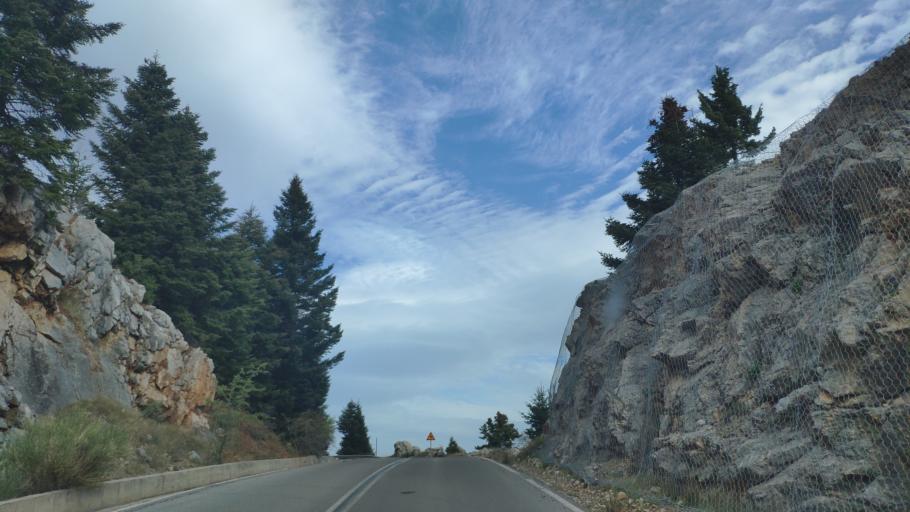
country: GR
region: Central Greece
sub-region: Nomos Fokidos
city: Amfissa
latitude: 38.6457
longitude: 22.3877
